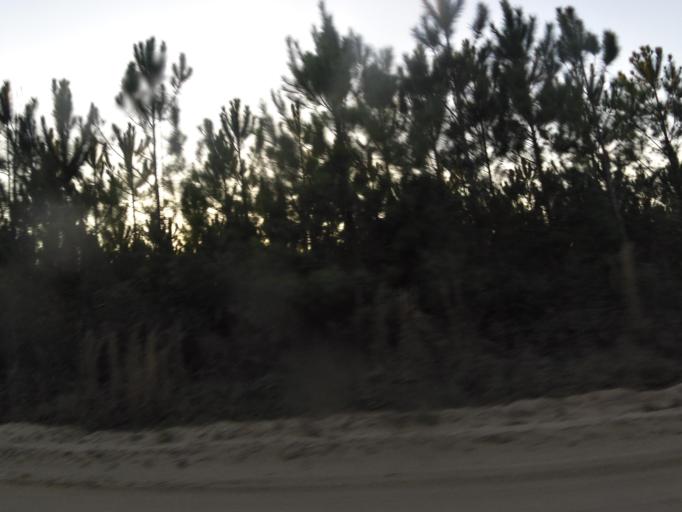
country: US
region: Florida
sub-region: Clay County
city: Green Cove Springs
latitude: 29.8870
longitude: -81.7901
